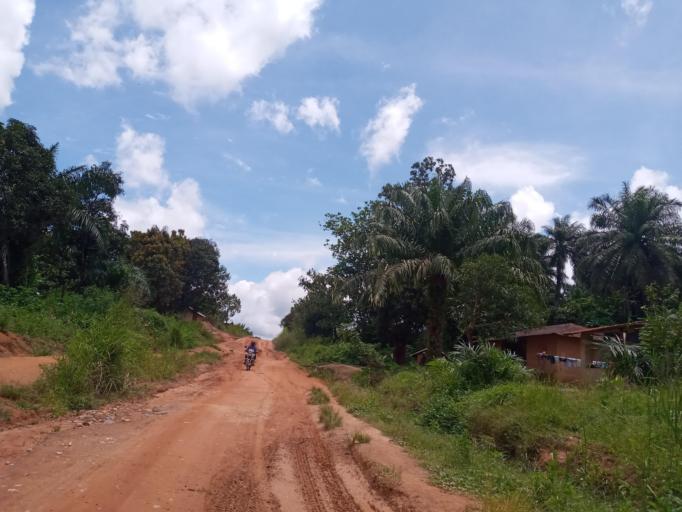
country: SL
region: Eastern Province
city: Koidu
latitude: 8.6448
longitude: -10.9178
